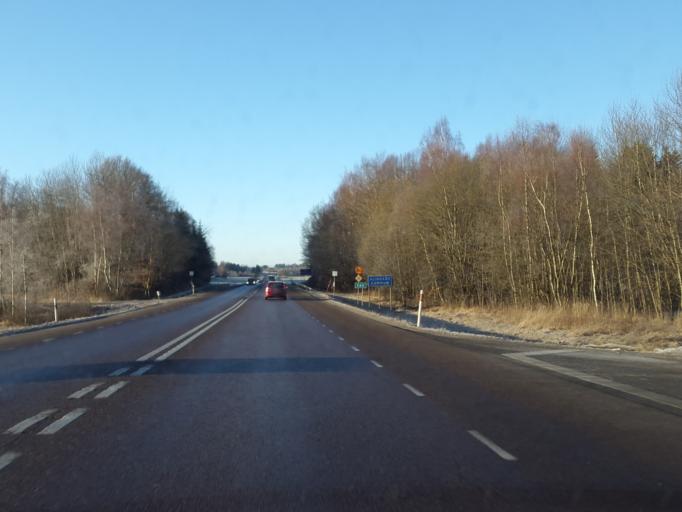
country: SE
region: Vaestra Goetaland
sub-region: Alingsas Kommun
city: Alingsas
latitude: 57.9627
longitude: 12.6208
